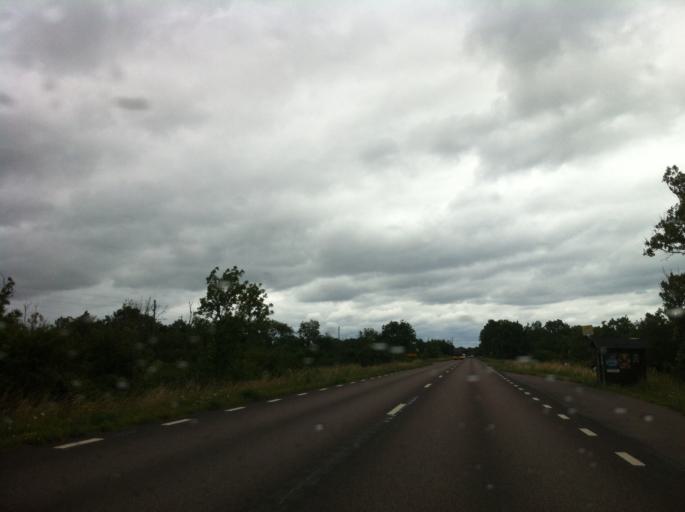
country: SE
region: Kalmar
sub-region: Borgholms Kommun
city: Borgholm
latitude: 57.1357
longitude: 16.9822
